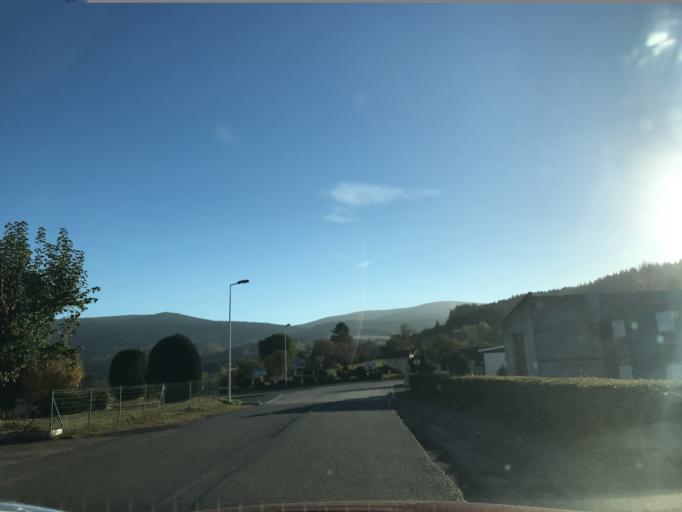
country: FR
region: Rhone-Alpes
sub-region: Departement de la Loire
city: Noiretable
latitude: 45.8172
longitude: 3.7578
